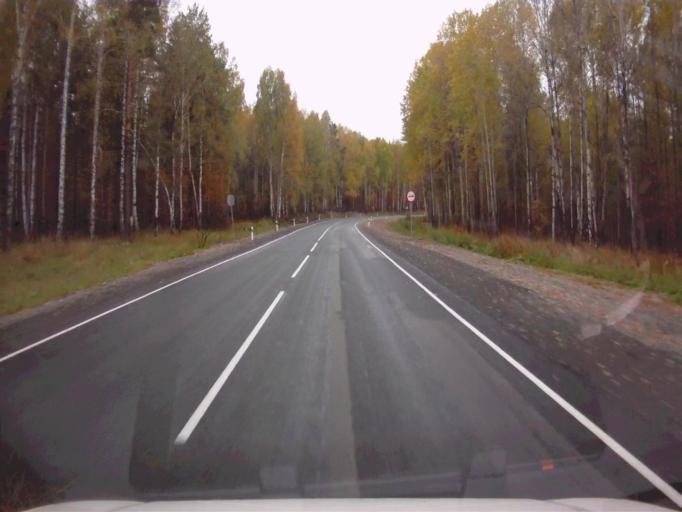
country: RU
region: Chelyabinsk
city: Nyazepetrovsk
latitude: 56.0612
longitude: 59.7294
